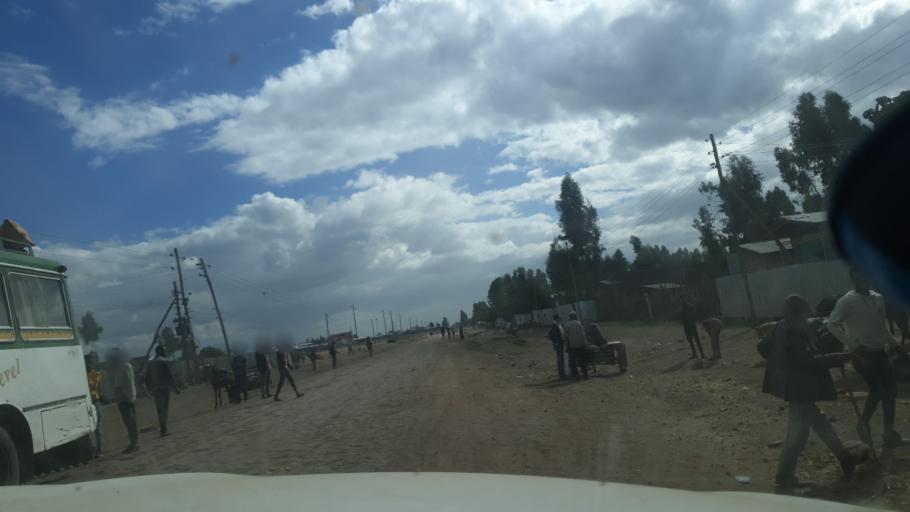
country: ET
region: Oromiya
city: Ziway
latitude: 7.7327
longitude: 39.0320
